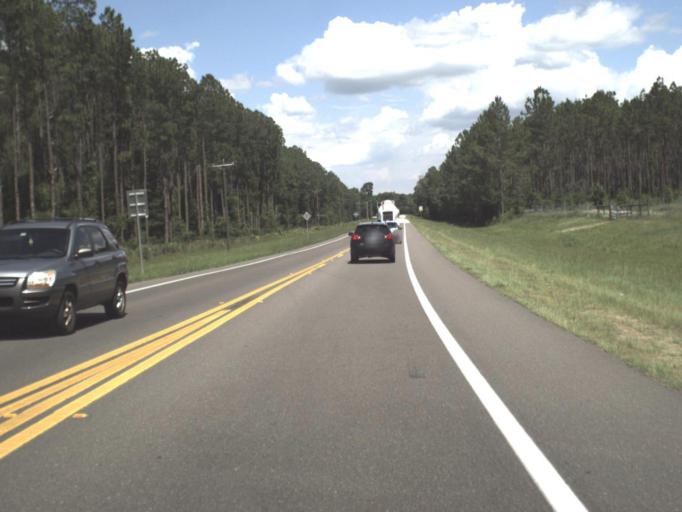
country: US
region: Florida
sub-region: Alachua County
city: Waldo
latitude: 29.7159
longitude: -82.1284
